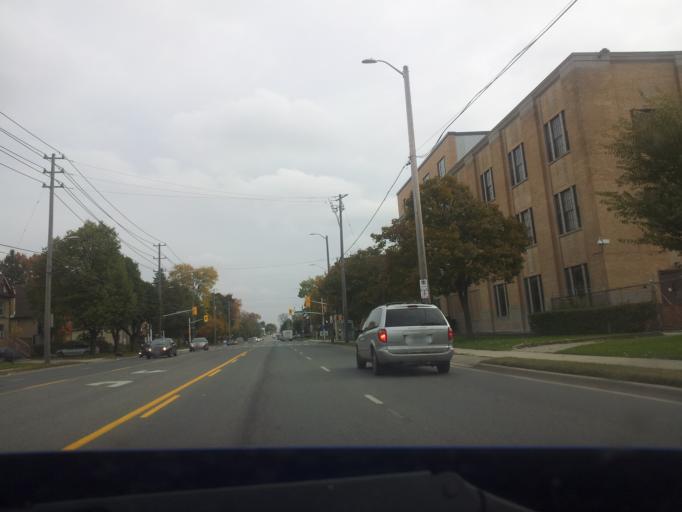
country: CA
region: Ontario
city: London
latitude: 42.9974
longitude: -81.2467
